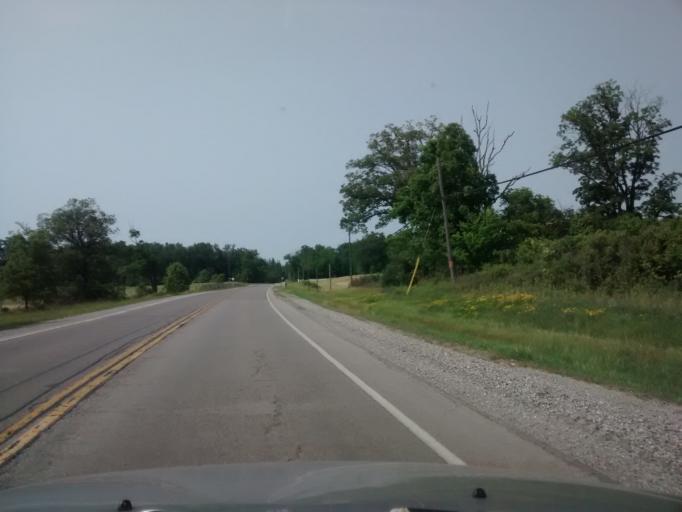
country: CA
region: Ontario
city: Ancaster
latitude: 42.9756
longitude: -79.8714
